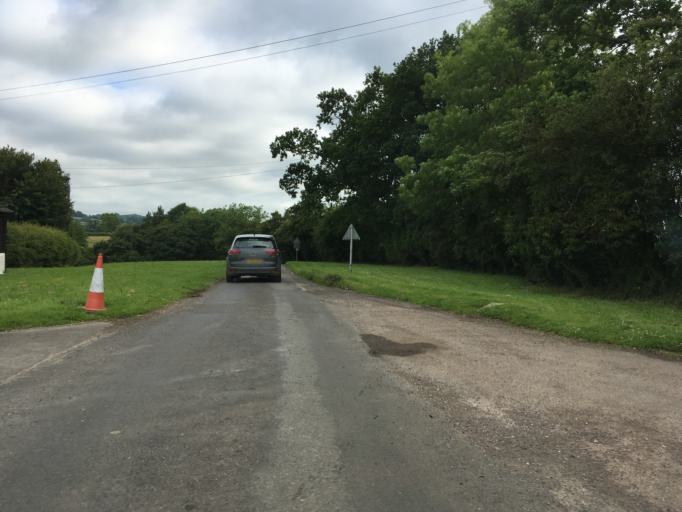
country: GB
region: England
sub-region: South Gloucestershire
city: Horton
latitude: 51.5763
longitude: -2.3507
